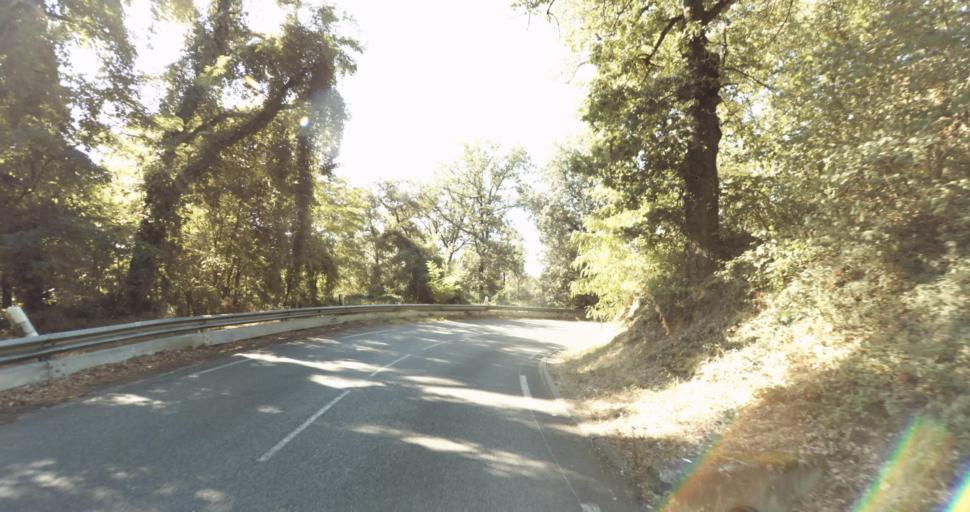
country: FR
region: Midi-Pyrenees
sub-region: Departement de la Haute-Garonne
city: Saint-Genies-Bellevue
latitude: 43.6745
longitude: 1.4782
